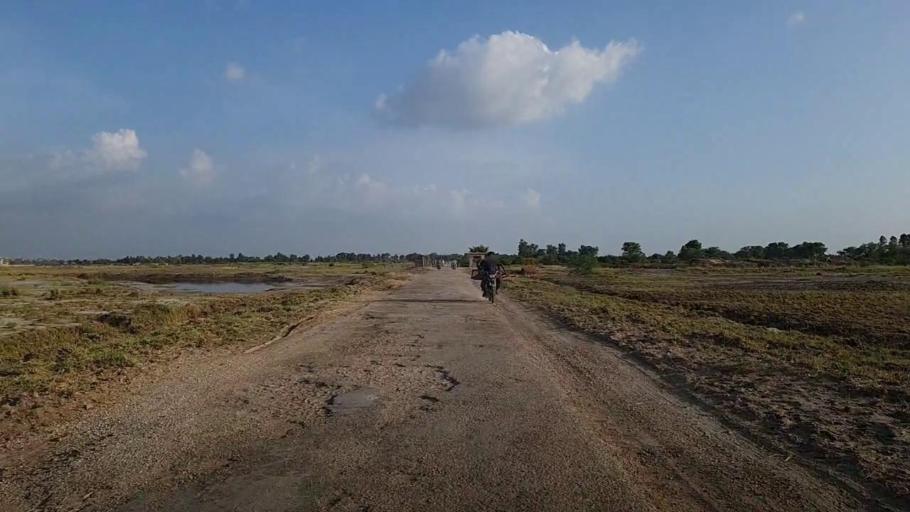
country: PK
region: Sindh
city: Hingorja
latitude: 27.0711
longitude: 68.4188
